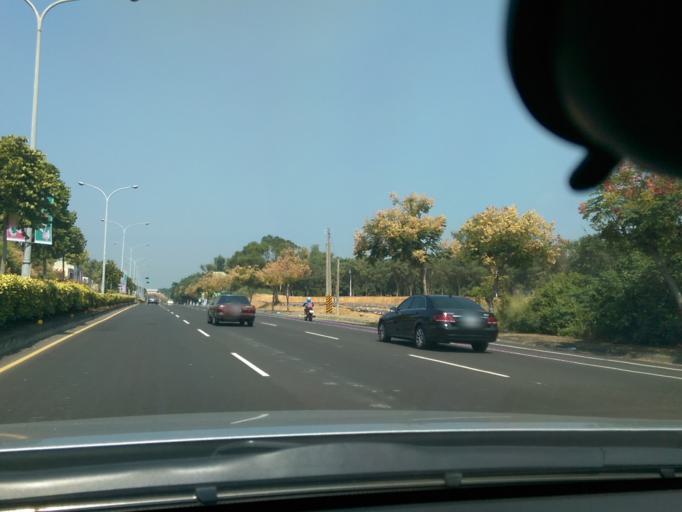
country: TW
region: Taiwan
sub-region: Chiayi
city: Jiayi Shi
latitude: 23.5388
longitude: 120.4352
